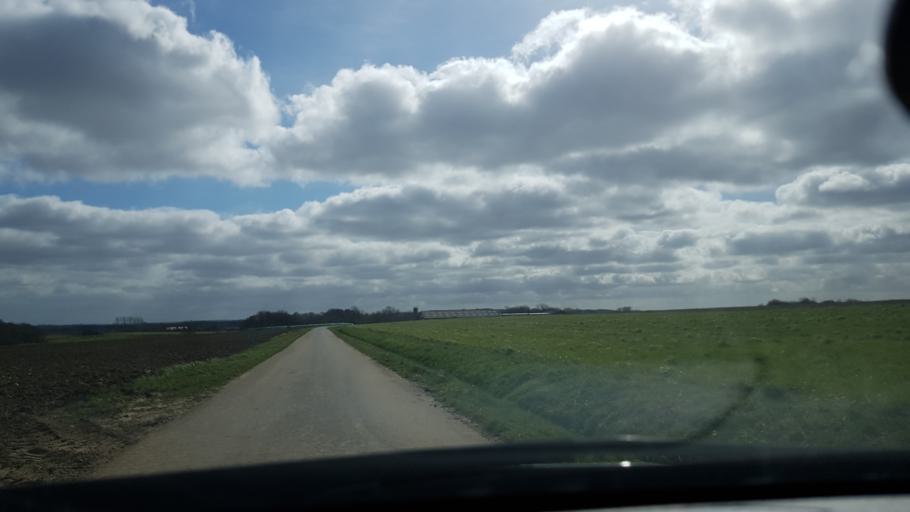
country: DK
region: South Denmark
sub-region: Haderslev Kommune
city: Gram
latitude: 55.3243
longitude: 8.9893
